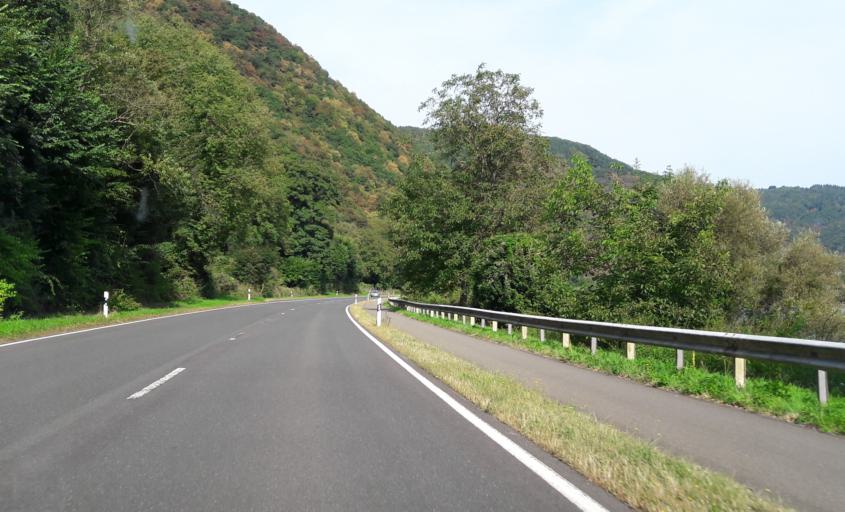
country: DE
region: Rheinland-Pfalz
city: Mesenich
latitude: 50.0940
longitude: 7.1946
